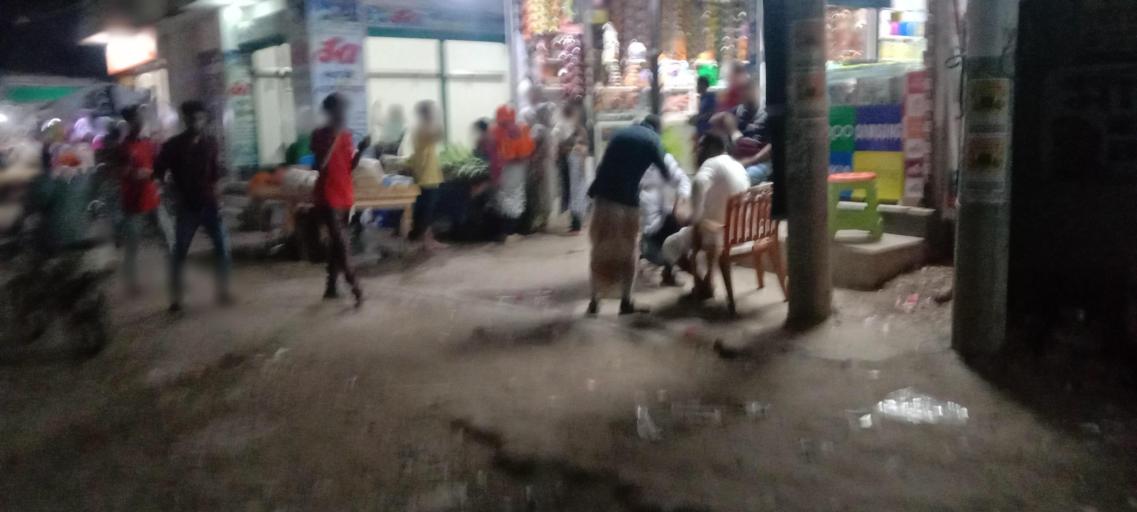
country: BD
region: Dhaka
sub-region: Dhaka
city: Dhaka
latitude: 23.6876
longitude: 90.3963
